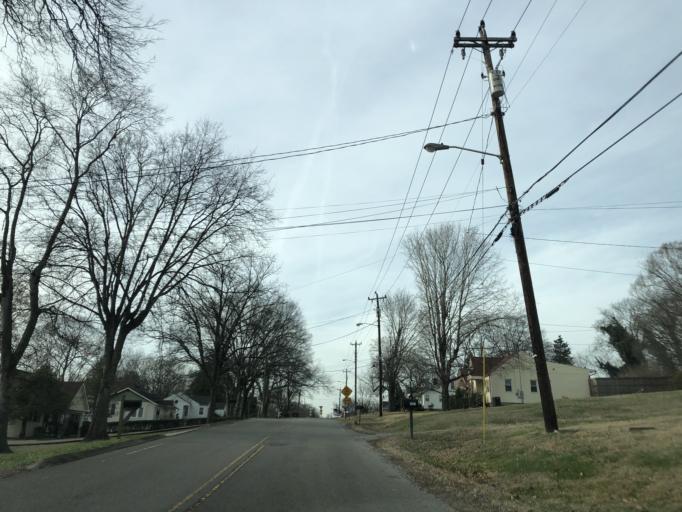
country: US
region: Tennessee
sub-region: Davidson County
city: Nashville
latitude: 36.2077
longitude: -86.7267
